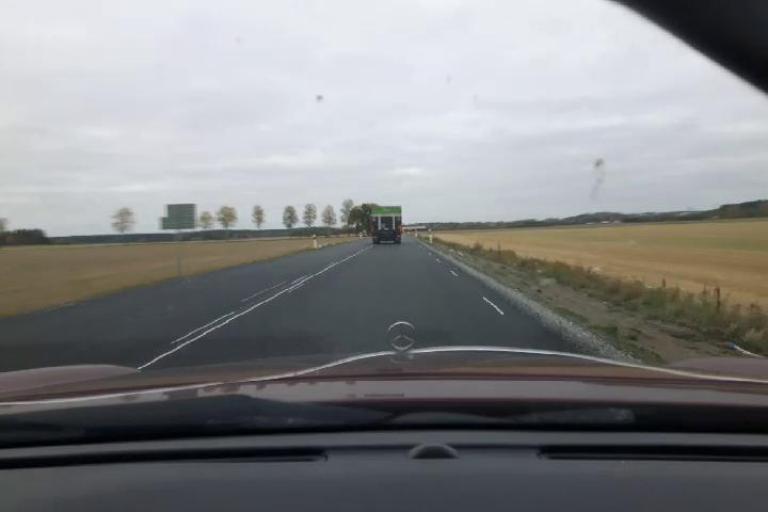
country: SE
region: Uppsala
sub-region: Enkopings Kommun
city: Enkoping
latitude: 59.6211
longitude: 17.0433
